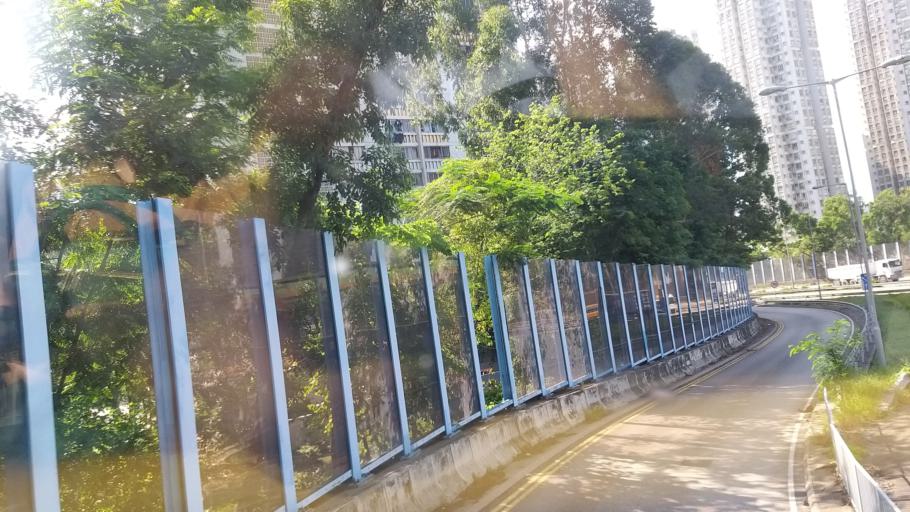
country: HK
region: Tuen Mun
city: Tuen Mun
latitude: 22.3866
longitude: 113.9717
